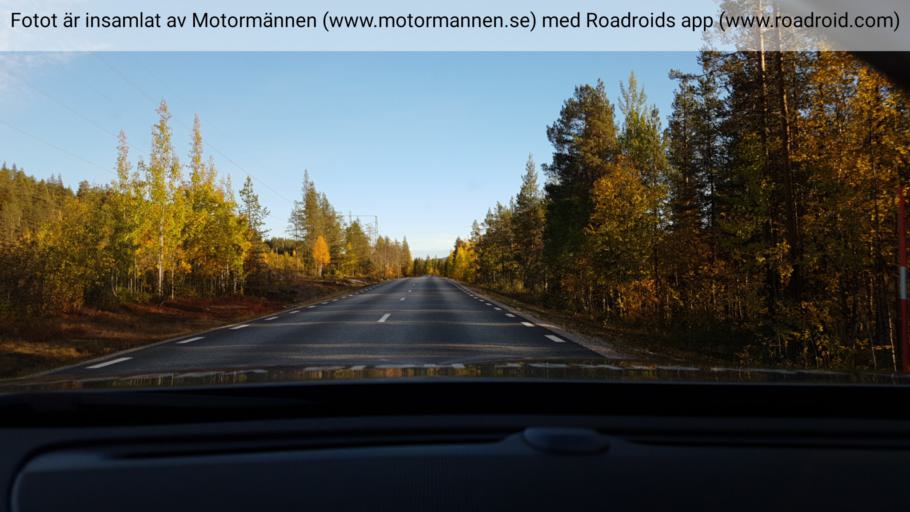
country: SE
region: Norrbotten
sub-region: Jokkmokks Kommun
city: Jokkmokk
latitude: 66.8275
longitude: 19.8598
